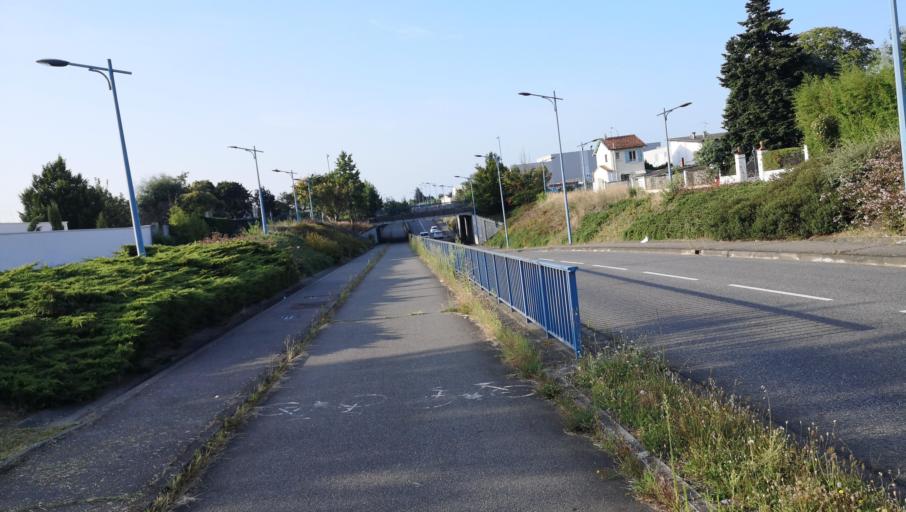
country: FR
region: Midi-Pyrenees
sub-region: Departement de la Haute-Garonne
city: Blagnac
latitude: 43.5975
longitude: 1.3930
